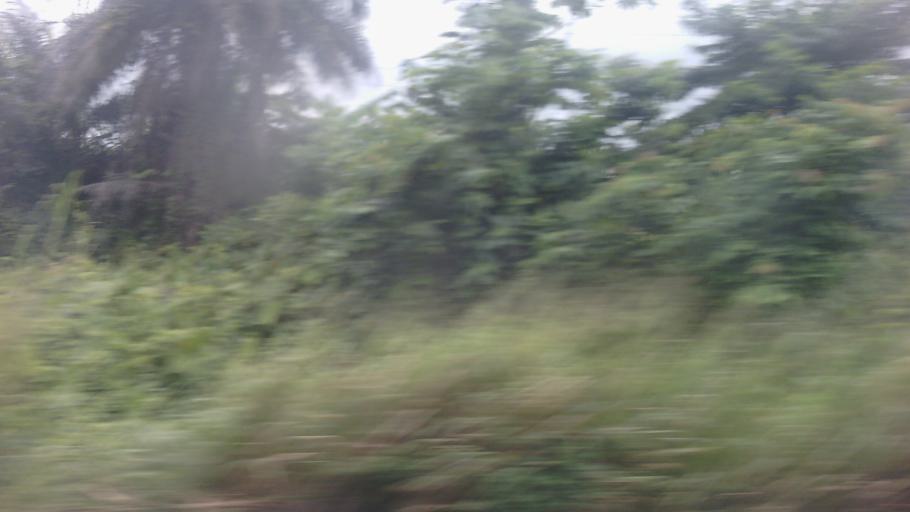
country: CI
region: Sud-Comoe
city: Aboisso
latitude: 5.4105
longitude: -3.2879
